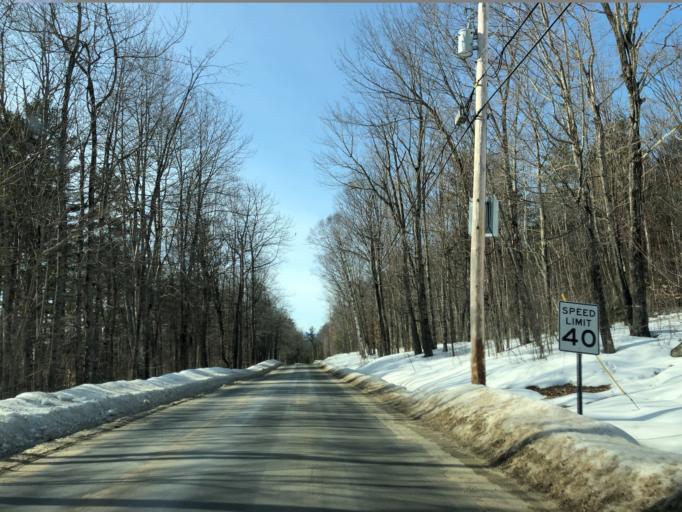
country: US
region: Maine
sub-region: Oxford County
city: Paris
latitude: 44.2670
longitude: -70.4738
